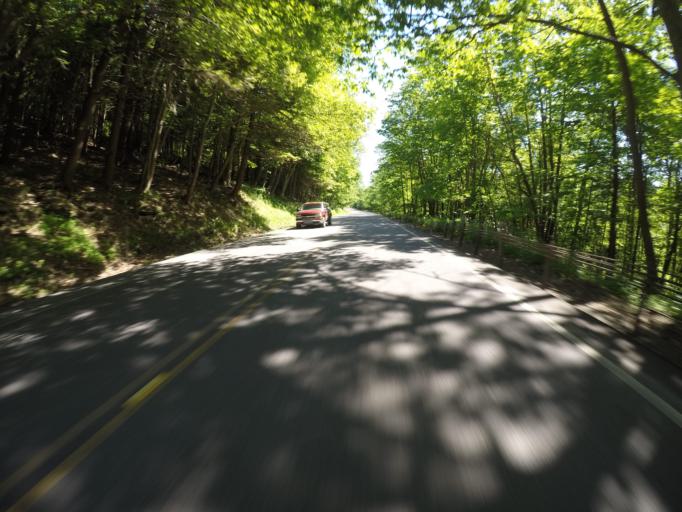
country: US
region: New York
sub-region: Delaware County
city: Delhi
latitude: 42.2585
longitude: -74.9348
